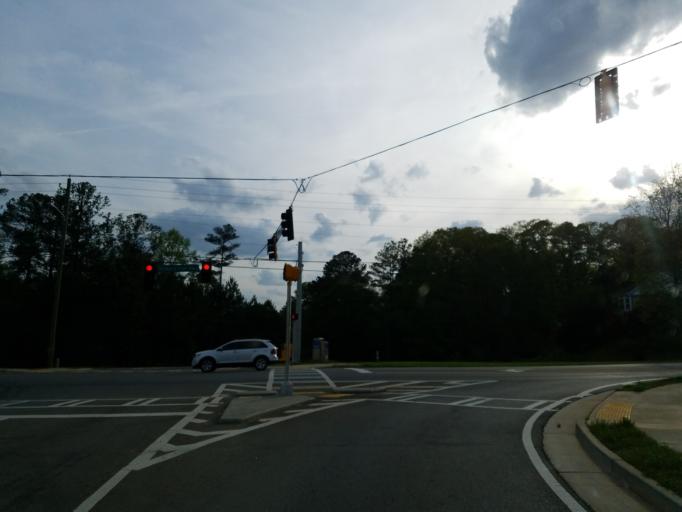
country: US
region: Georgia
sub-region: Cherokee County
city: Canton
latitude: 34.2186
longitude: -84.4607
